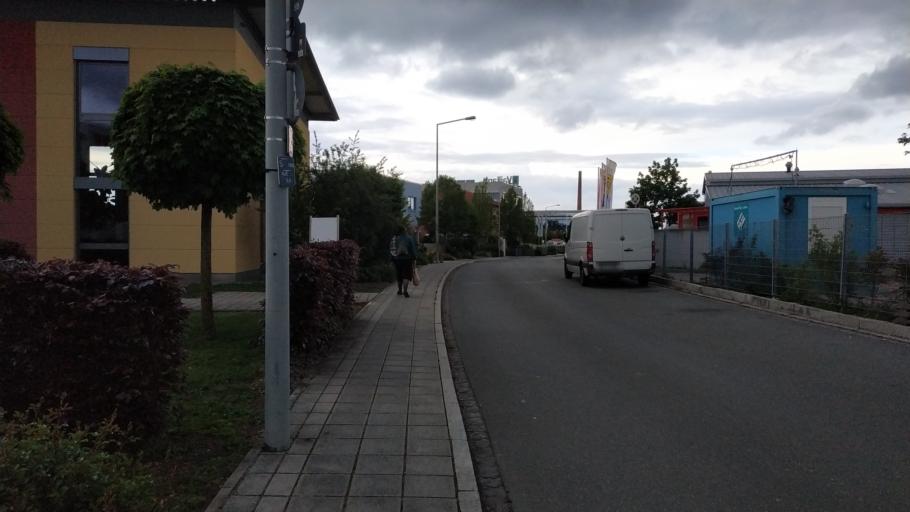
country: DE
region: Bavaria
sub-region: Regierungsbezirk Mittelfranken
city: Grossreuth bei Schweinau
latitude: 49.4266
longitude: 11.0562
